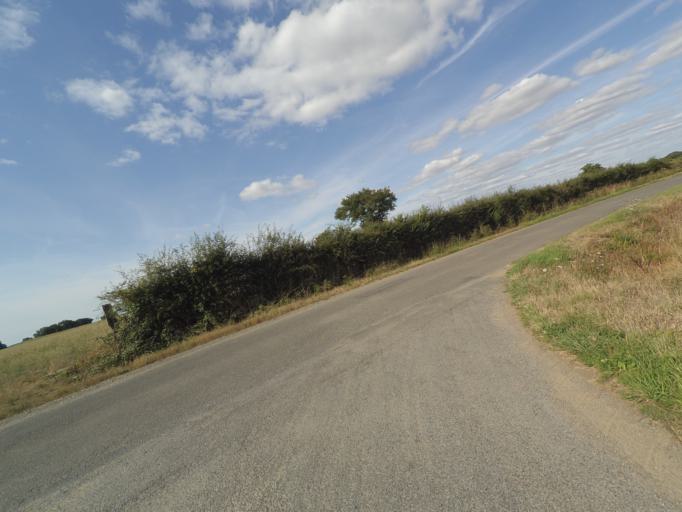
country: FR
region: Pays de la Loire
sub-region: Departement de la Loire-Atlantique
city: Vieillevigne
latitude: 46.9576
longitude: -1.4459
